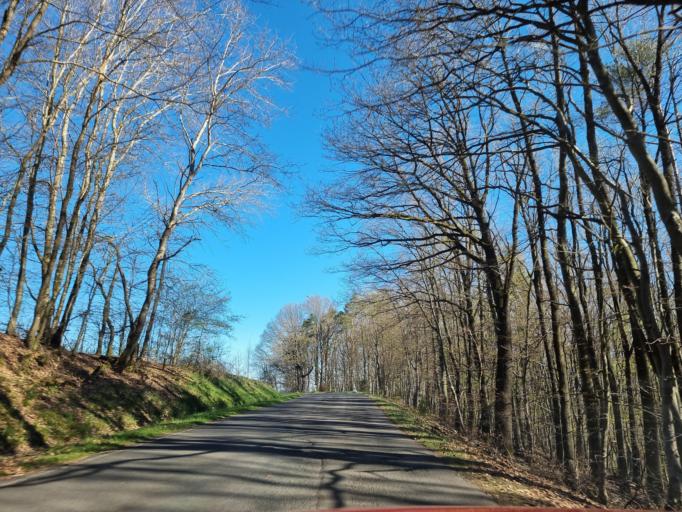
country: DE
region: Rheinland-Pfalz
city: Dierscheid
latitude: 49.8952
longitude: 6.7630
